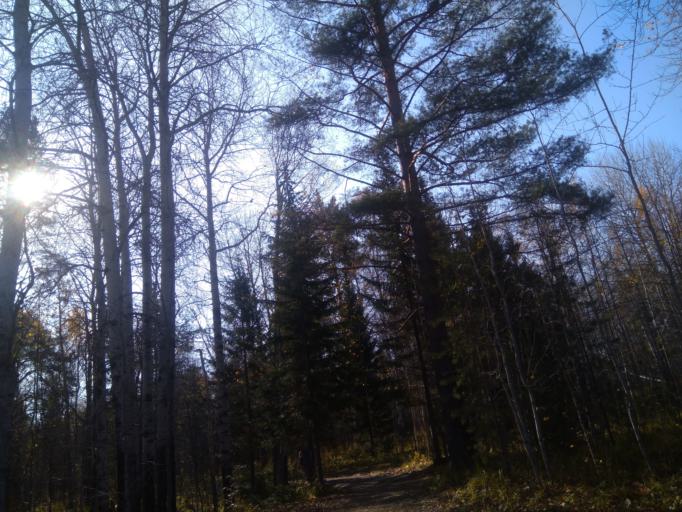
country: RU
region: Sverdlovsk
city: Mikhaylovsk
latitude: 56.5214
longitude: 59.2348
